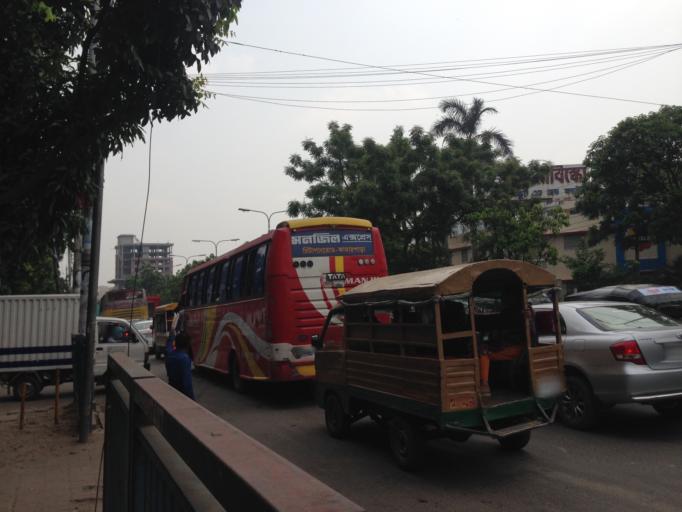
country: BD
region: Dhaka
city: Paltan
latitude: 23.7685
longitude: 90.4006
